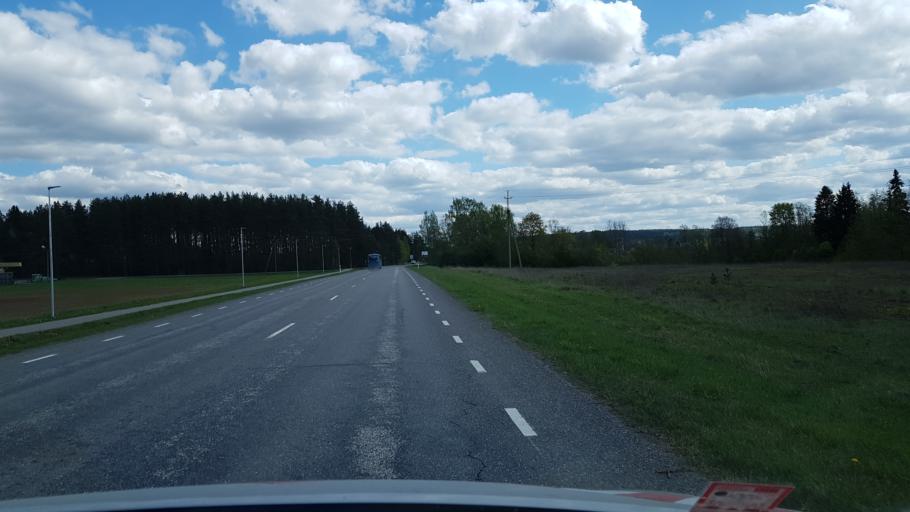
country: EE
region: Tartu
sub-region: UElenurme vald
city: Ulenurme
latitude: 58.3043
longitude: 26.8603
